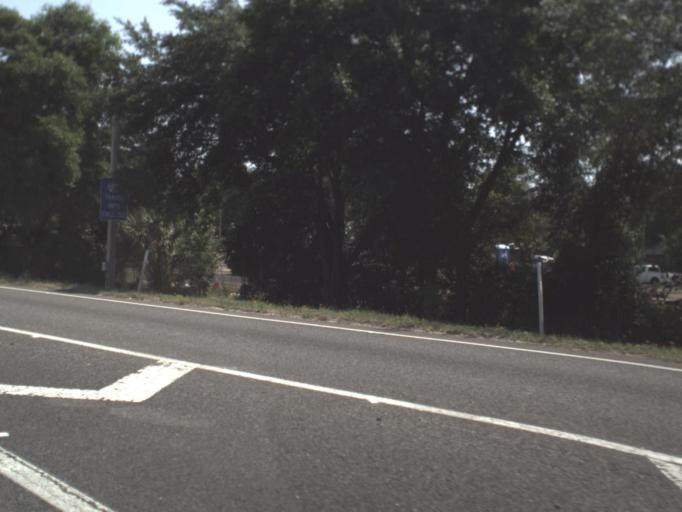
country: US
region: Florida
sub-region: Duval County
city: Jacksonville
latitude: 30.3390
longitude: -81.6681
